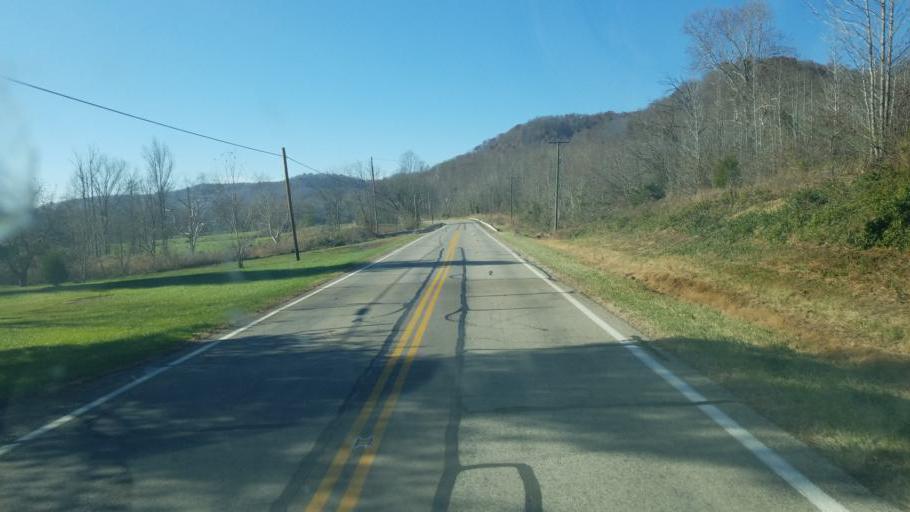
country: US
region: Kentucky
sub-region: Lewis County
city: Vanceburg
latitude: 38.6381
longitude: -83.2328
